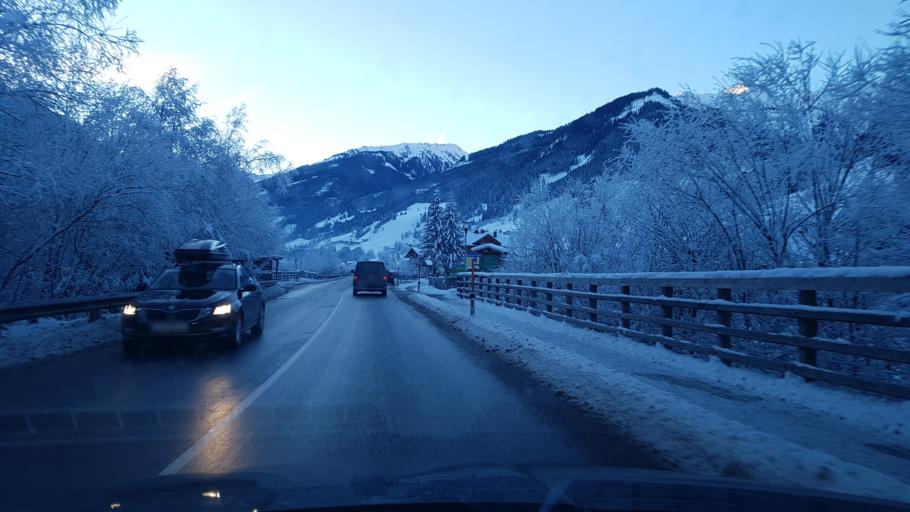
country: AT
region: Salzburg
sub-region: Politischer Bezirk Sankt Johann im Pongau
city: Huttschlag
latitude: 47.2213
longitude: 13.1967
